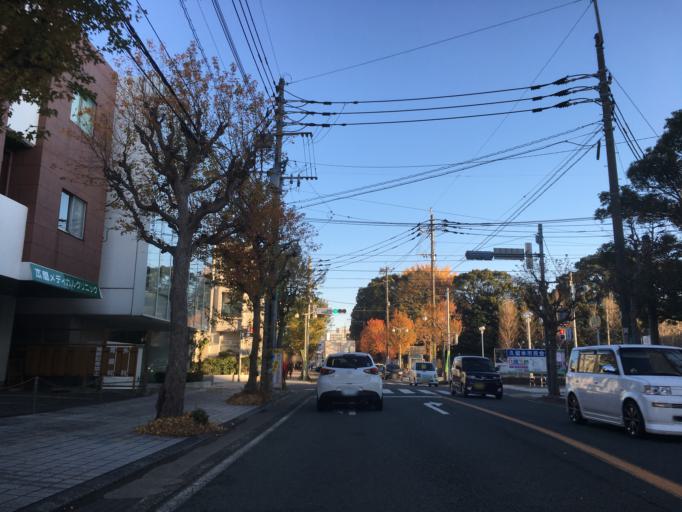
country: JP
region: Fukuoka
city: Kurume
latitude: 33.3195
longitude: 130.5076
